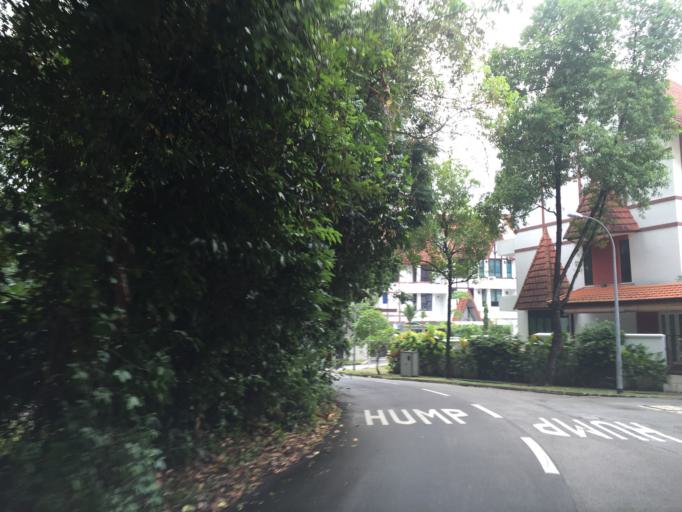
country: SG
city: Singapore
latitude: 1.3220
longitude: 103.8338
